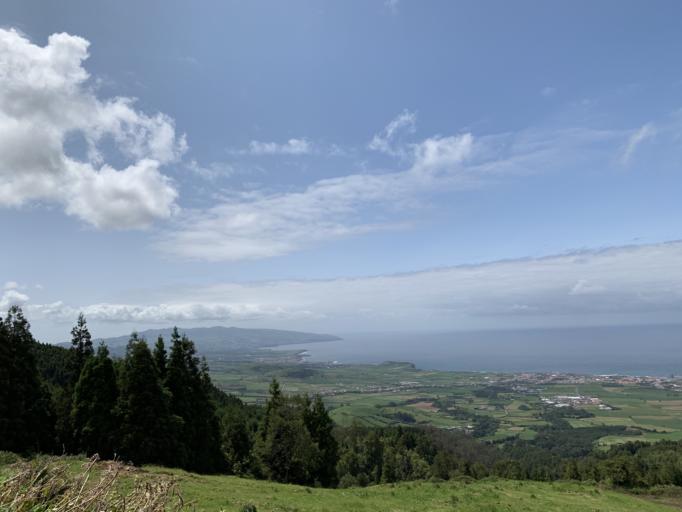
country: PT
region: Azores
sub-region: Vila Franca do Campo
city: Vila Franca do Campo
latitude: 37.7782
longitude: -25.4955
